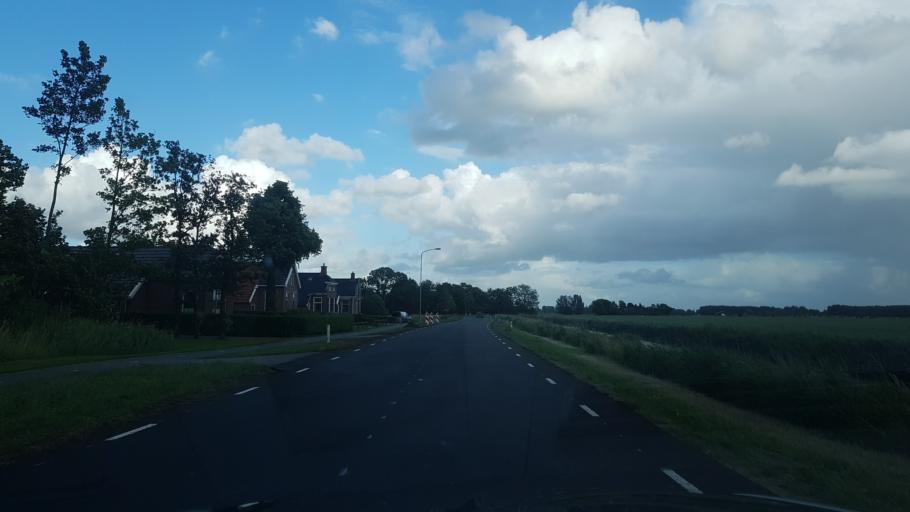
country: NL
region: Groningen
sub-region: Gemeente Appingedam
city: Appingedam
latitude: 53.3245
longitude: 6.7573
